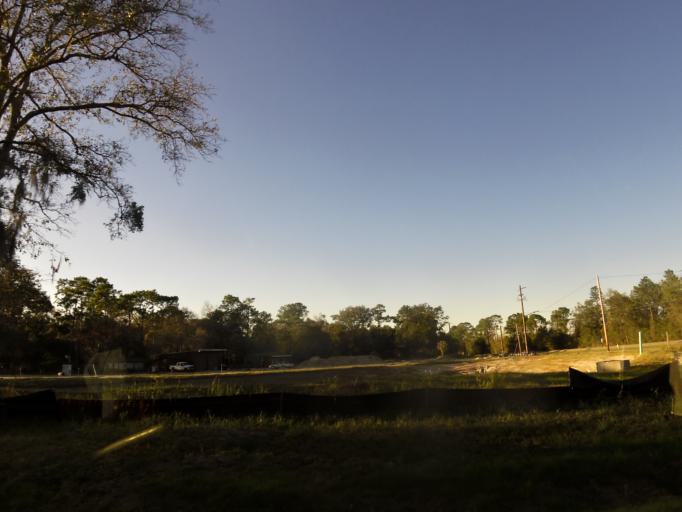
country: US
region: Florida
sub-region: Saint Johns County
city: Fruit Cove
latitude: 30.1994
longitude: -81.5746
